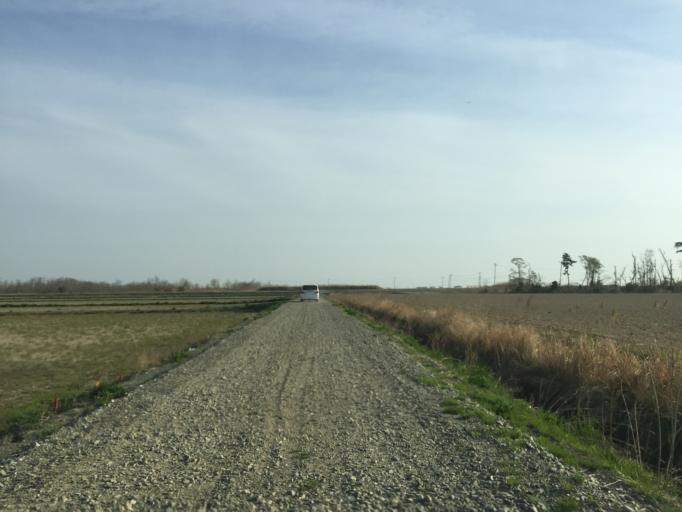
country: JP
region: Miyagi
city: Watari
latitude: 38.0260
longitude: 140.9121
